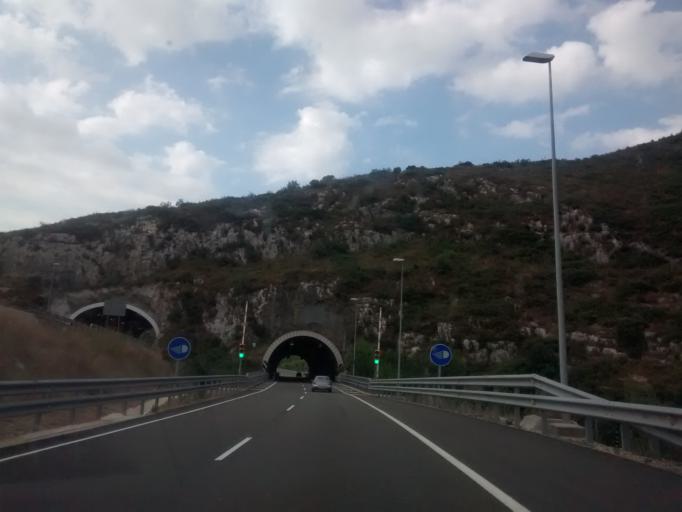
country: ES
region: Catalonia
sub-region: Provincia de Barcelona
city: Vilafranca del Penedes
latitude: 41.3094
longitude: 1.7219
